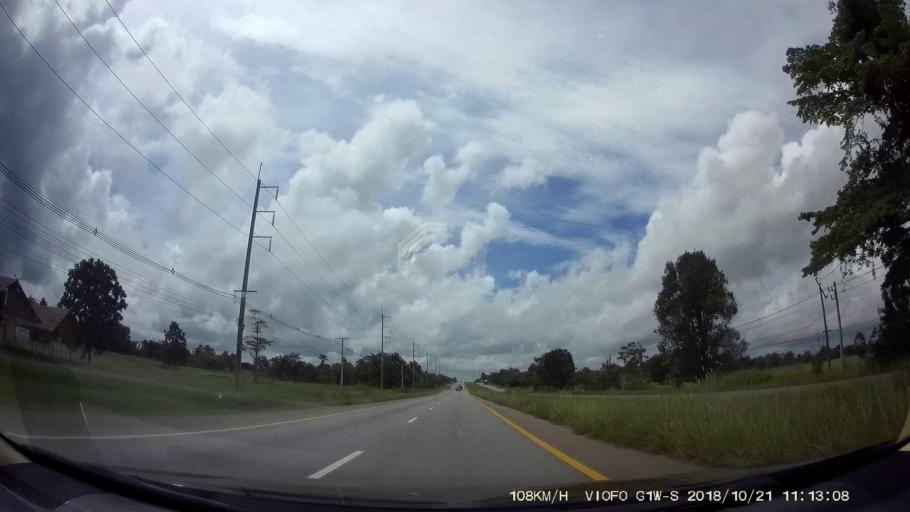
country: TH
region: Chaiyaphum
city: Khon Sawan
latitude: 15.9202
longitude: 102.1364
